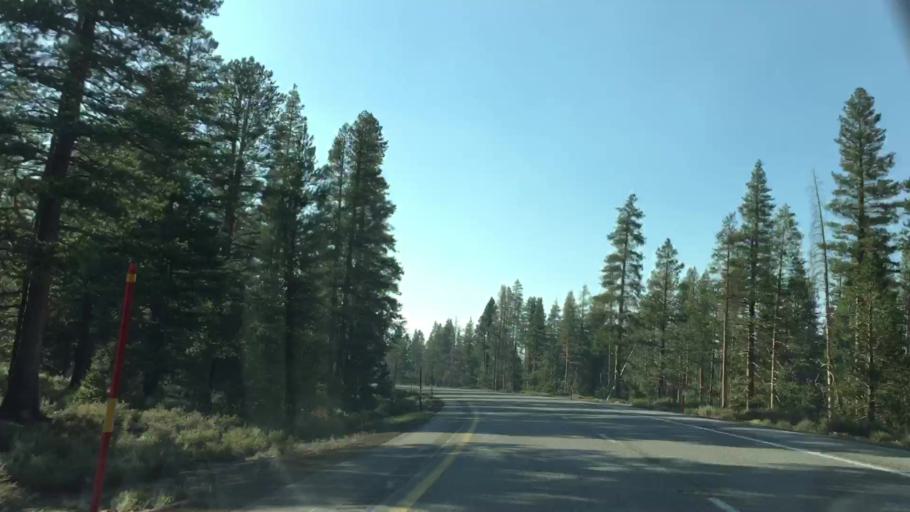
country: US
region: California
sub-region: Mono County
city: Mammoth Lakes
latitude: 37.7869
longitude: -119.0232
